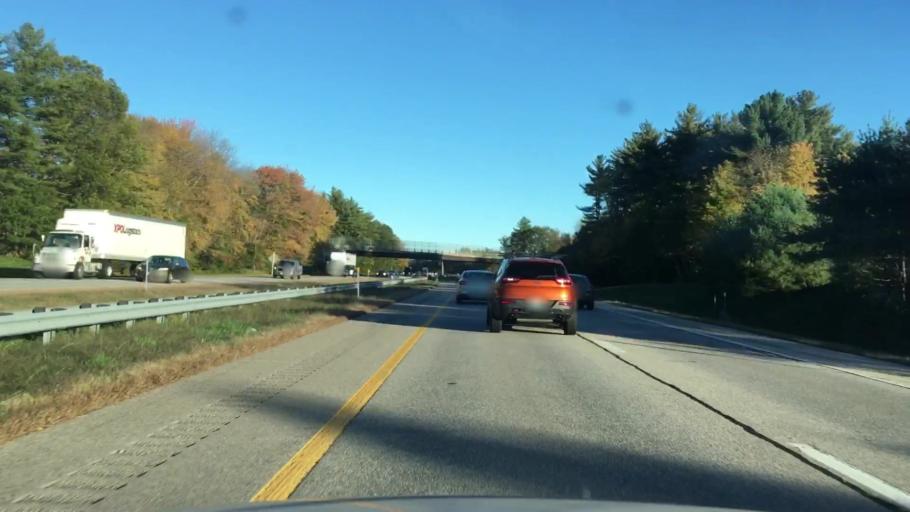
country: US
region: New Hampshire
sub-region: Rockingham County
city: Fremont
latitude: 43.0276
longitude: -71.1198
